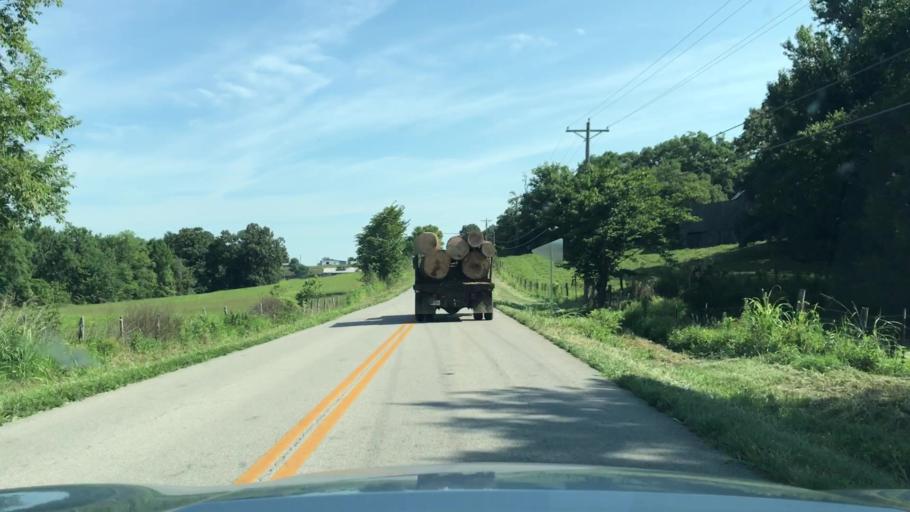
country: US
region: Kentucky
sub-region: Clinton County
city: Albany
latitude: 36.7617
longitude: -84.9971
